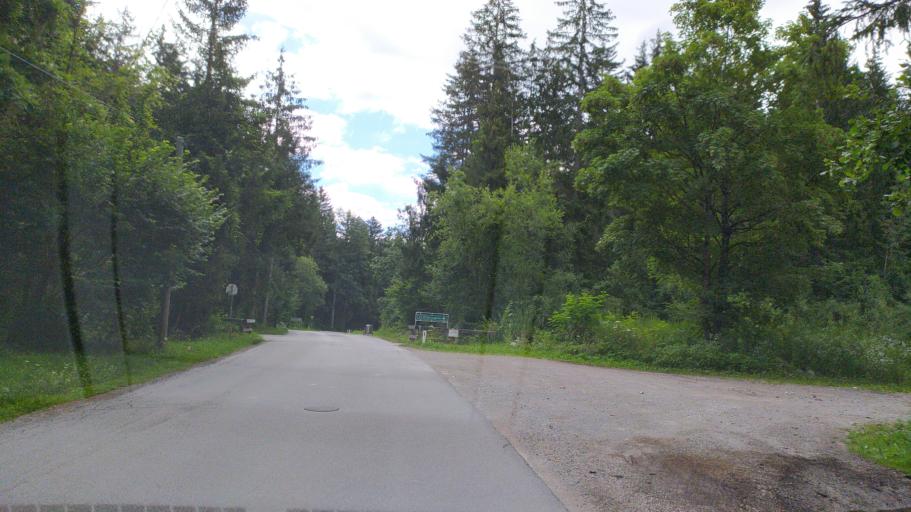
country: AT
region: Tyrol
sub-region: Politischer Bezirk Lienz
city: Tristach
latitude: 46.8133
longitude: 12.8154
